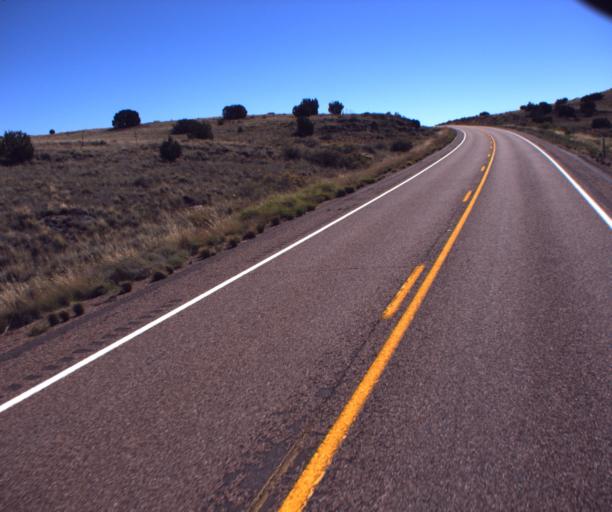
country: US
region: Arizona
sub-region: Apache County
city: Saint Johns
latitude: 34.5628
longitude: -109.5051
